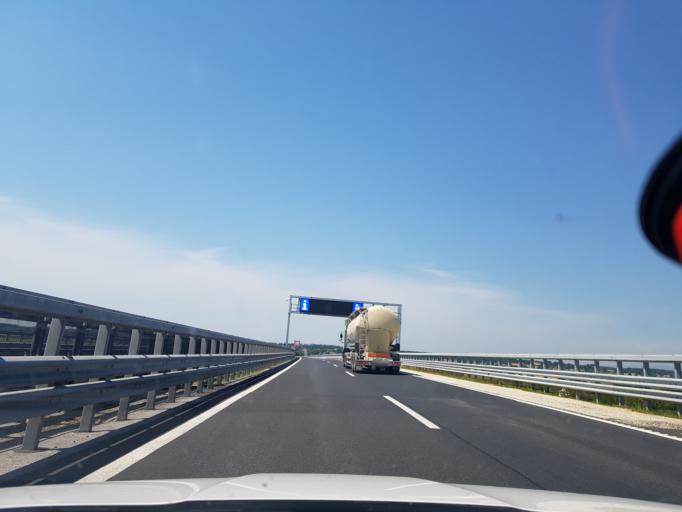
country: HU
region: Vas
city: Sarvar
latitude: 47.3212
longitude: 16.8514
